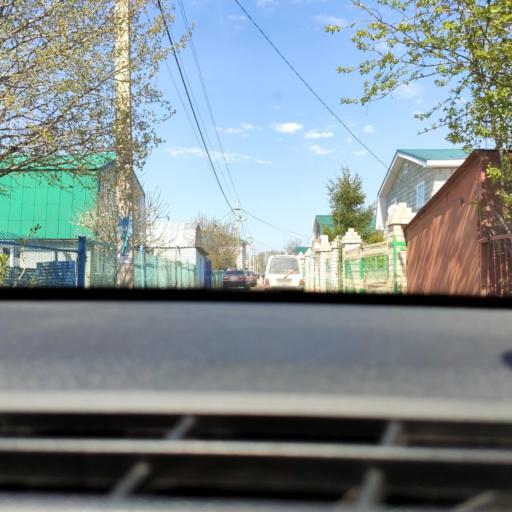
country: RU
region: Samara
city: Tol'yatti
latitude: 53.5952
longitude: 49.3012
